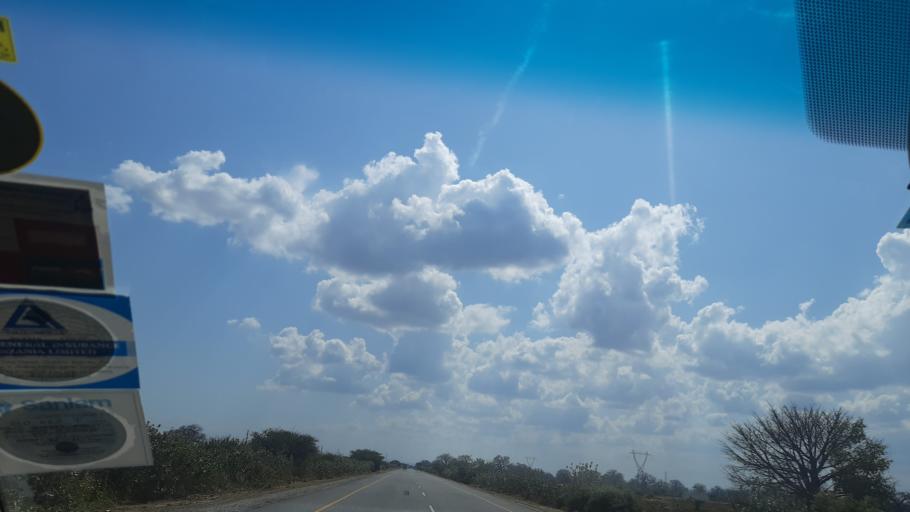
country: TZ
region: Singida
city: Kintinku
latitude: -5.9301
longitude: 35.2764
